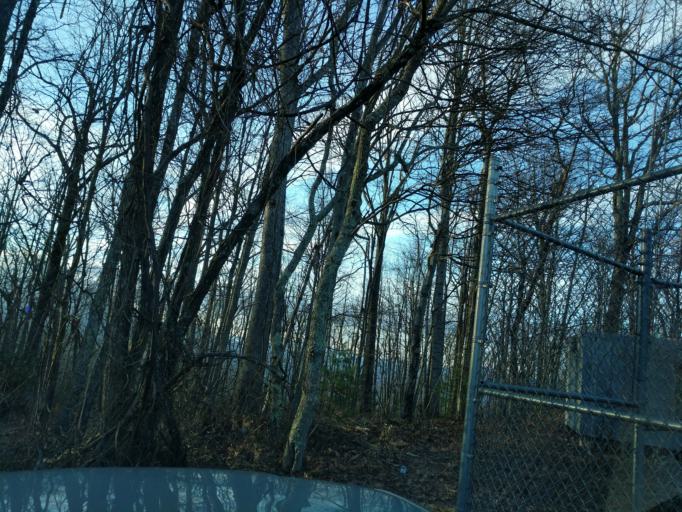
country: US
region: North Carolina
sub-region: Haywood County
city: Cove Creek
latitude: 35.7336
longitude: -83.0514
